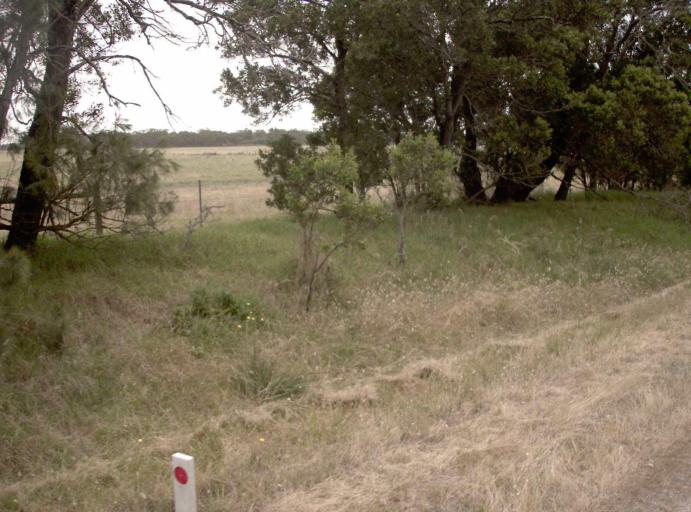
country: AU
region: Victoria
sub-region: Wellington
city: Sale
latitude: -38.1993
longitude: 147.3351
